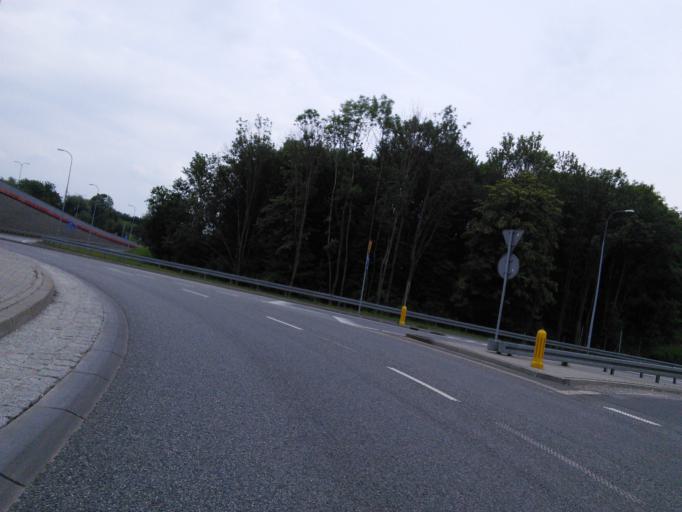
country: PL
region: Silesian Voivodeship
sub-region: Piekary Slaskie
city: Piekary Slaskie
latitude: 50.3658
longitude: 18.9379
